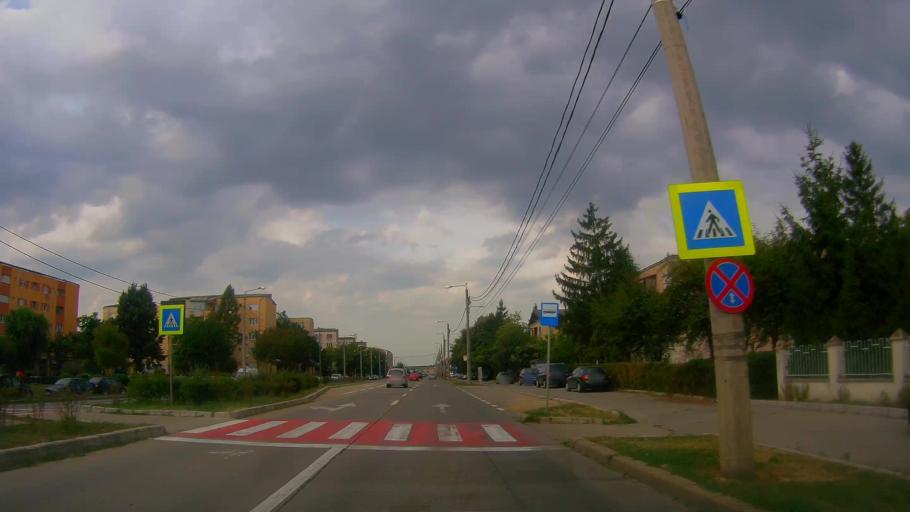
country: RO
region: Satu Mare
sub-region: Comuna Paulesti
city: Paulesti
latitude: 47.8016
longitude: 22.9053
